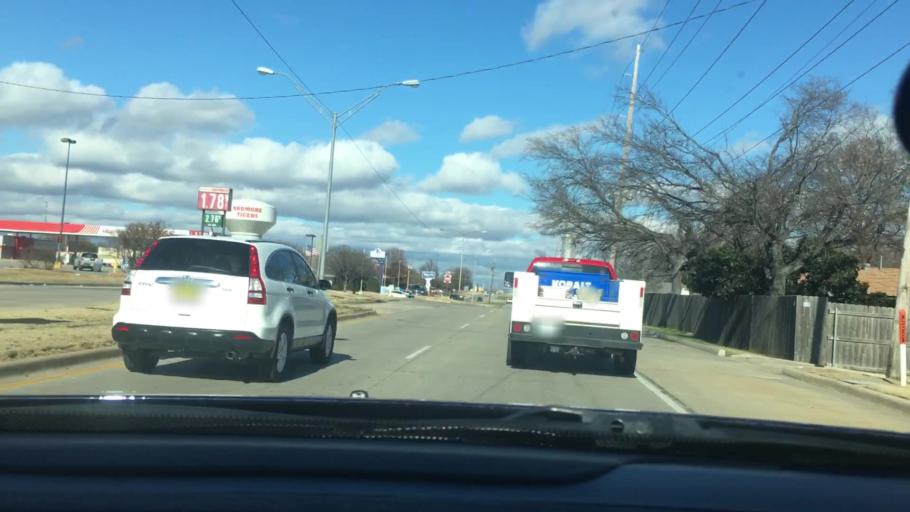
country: US
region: Oklahoma
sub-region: Carter County
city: Ardmore
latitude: 34.1931
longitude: -97.1430
